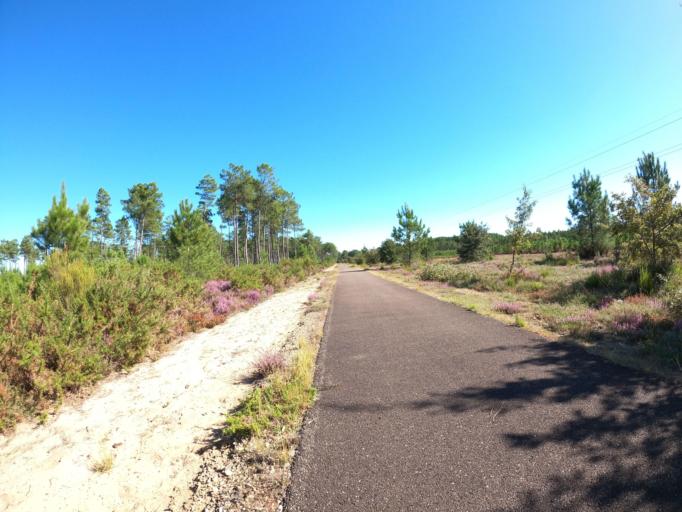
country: FR
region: Aquitaine
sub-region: Departement des Landes
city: Ychoux
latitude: 44.3376
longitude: -0.9552
